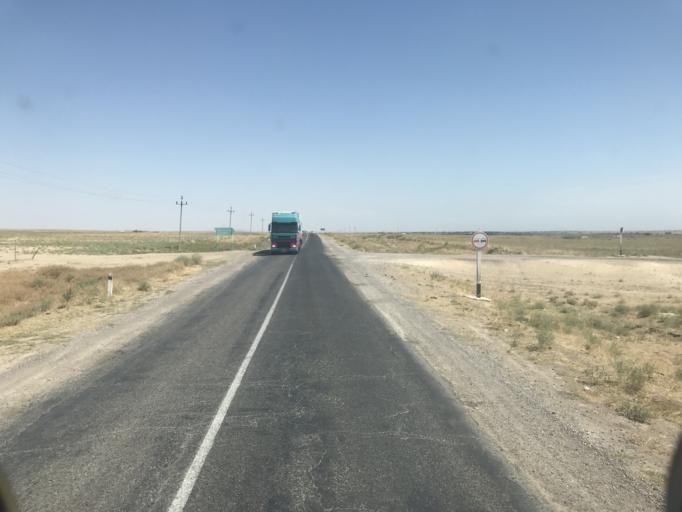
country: UZ
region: Toshkent
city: Amir Timur
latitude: 41.3625
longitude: 68.7294
